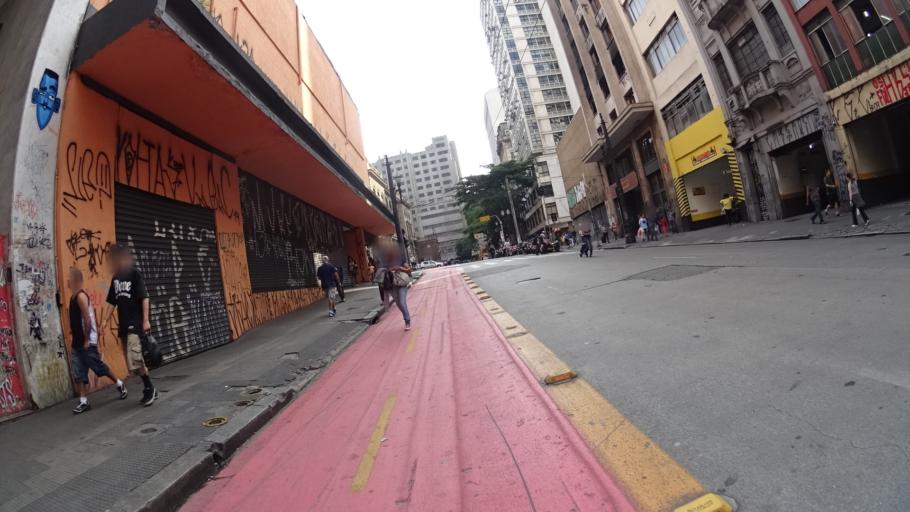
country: BR
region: Sao Paulo
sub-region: Sao Paulo
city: Sao Paulo
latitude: -23.5442
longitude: -46.6382
